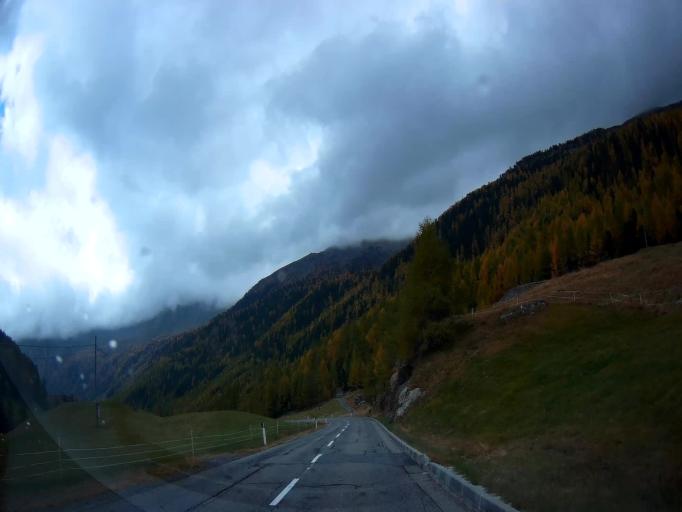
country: IT
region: Trentino-Alto Adige
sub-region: Bolzano
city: Silandro
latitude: 46.7450
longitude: 10.7882
